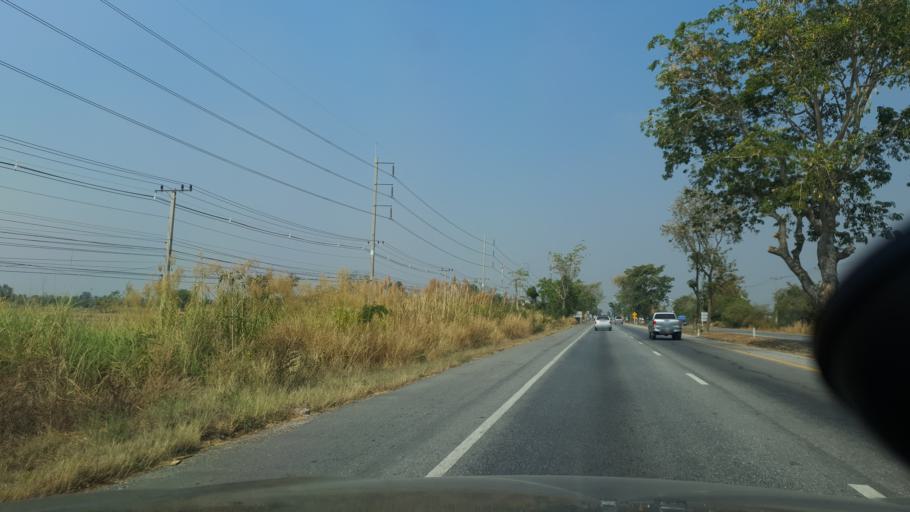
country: TH
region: Kamphaeng Phet
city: Khanu Woralaksaburi
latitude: 16.0696
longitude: 99.7333
